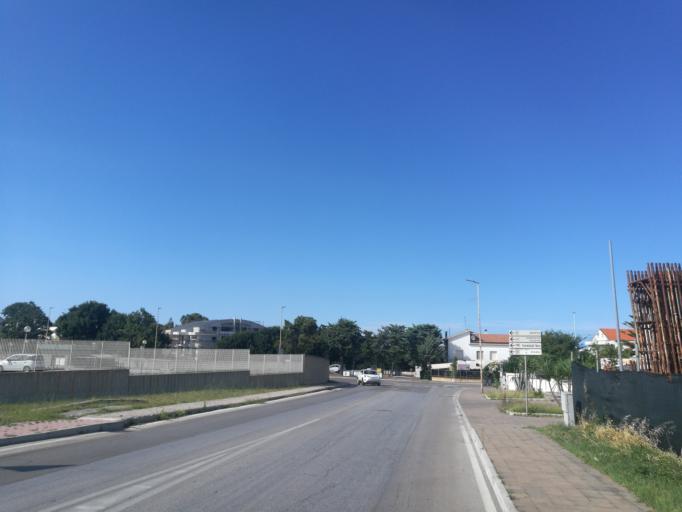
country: IT
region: Molise
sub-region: Provincia di Campobasso
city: Termoli
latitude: 41.9880
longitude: 14.9934
